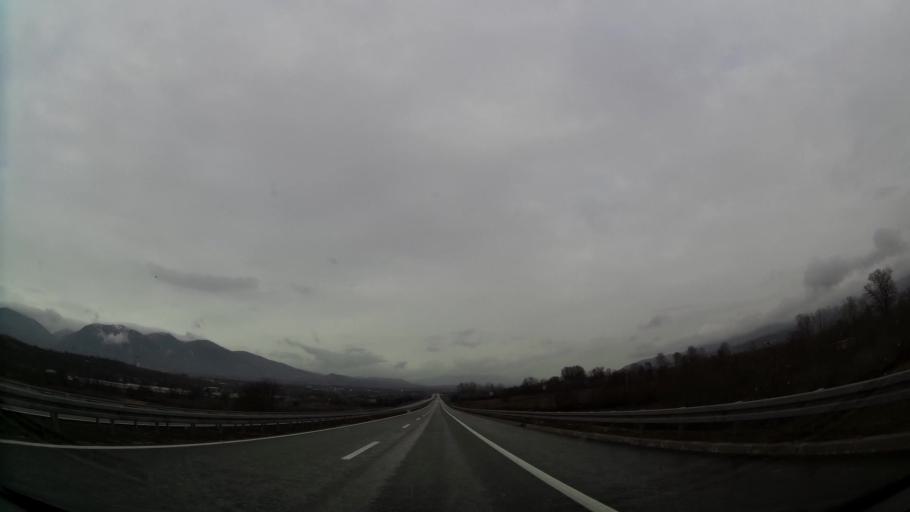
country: RS
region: Central Serbia
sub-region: Pcinjski Okrug
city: Vranje
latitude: 42.5278
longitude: 21.9204
